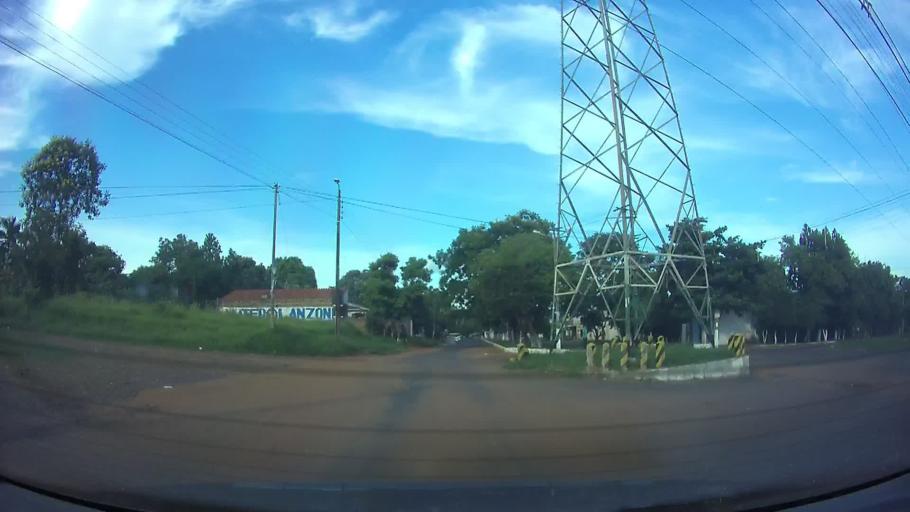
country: PY
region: Central
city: San Antonio
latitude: -25.4234
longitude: -57.5408
